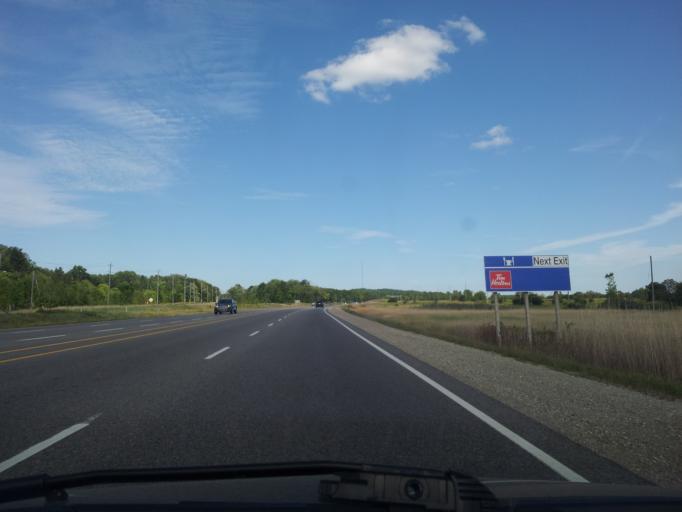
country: CA
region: Ontario
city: Kitchener
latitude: 43.3868
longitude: -80.6799
